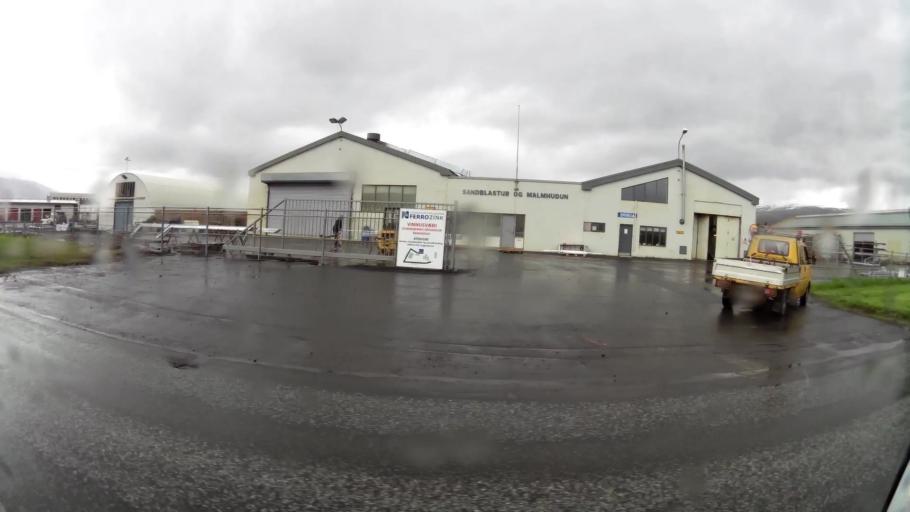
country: IS
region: Northeast
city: Akureyri
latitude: 65.6924
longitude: -18.0960
